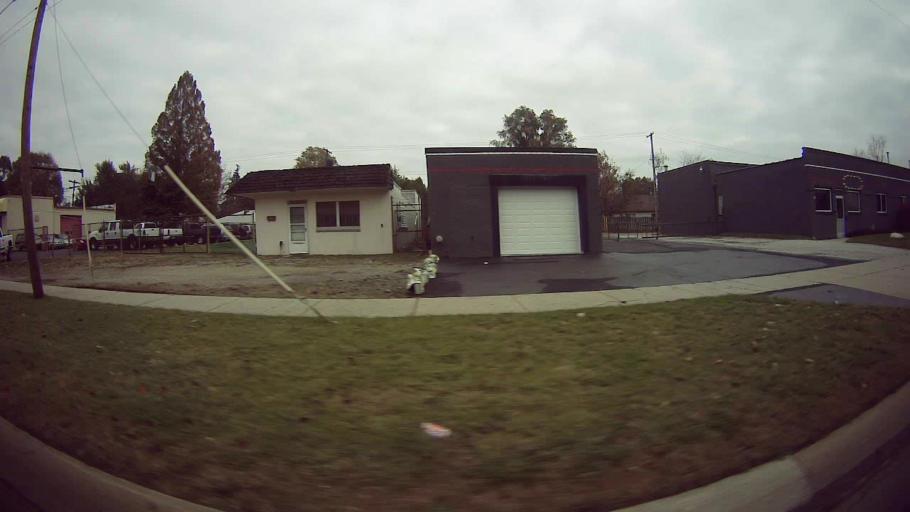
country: US
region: Michigan
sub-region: Oakland County
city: Hazel Park
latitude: 42.4495
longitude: -83.0636
